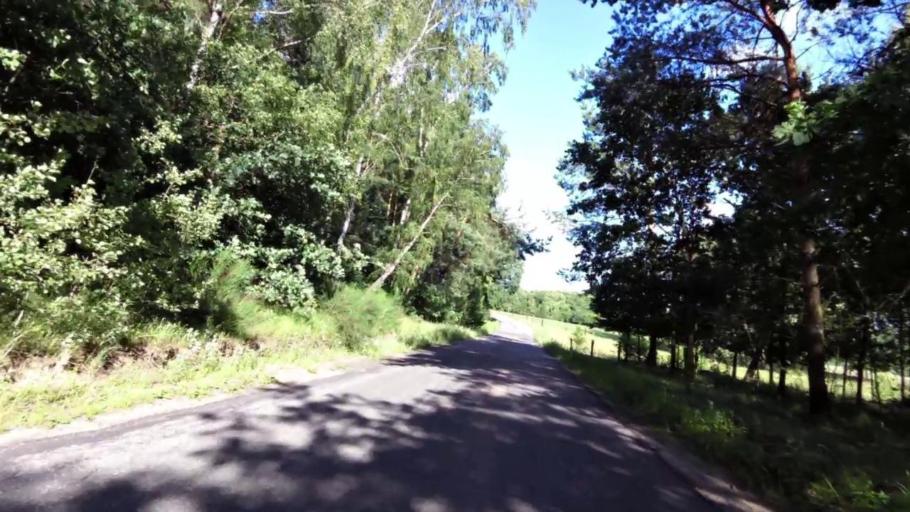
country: PL
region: West Pomeranian Voivodeship
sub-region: Powiat slawienski
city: Slawno
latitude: 54.4361
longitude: 16.7606
